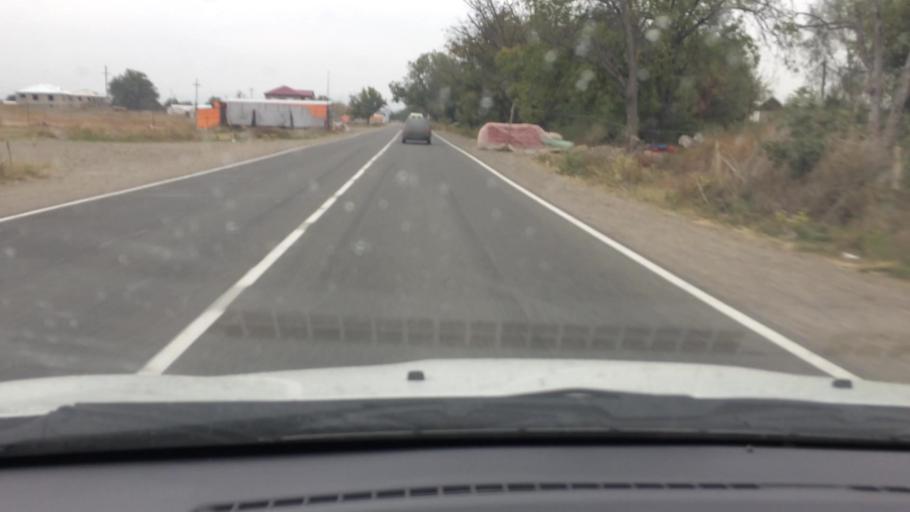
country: GE
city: Naghvarevi
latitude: 41.3958
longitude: 44.8268
